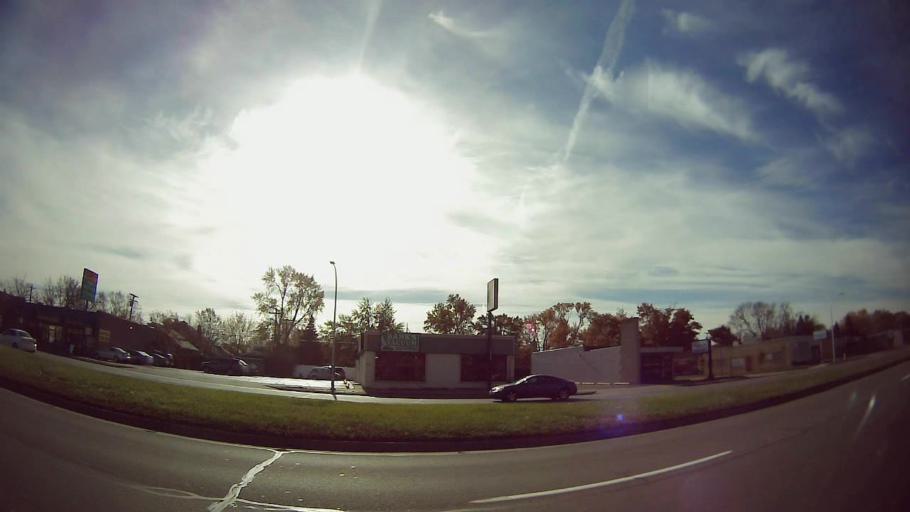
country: US
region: Michigan
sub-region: Wayne County
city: Dearborn Heights
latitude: 42.3272
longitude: -83.2644
